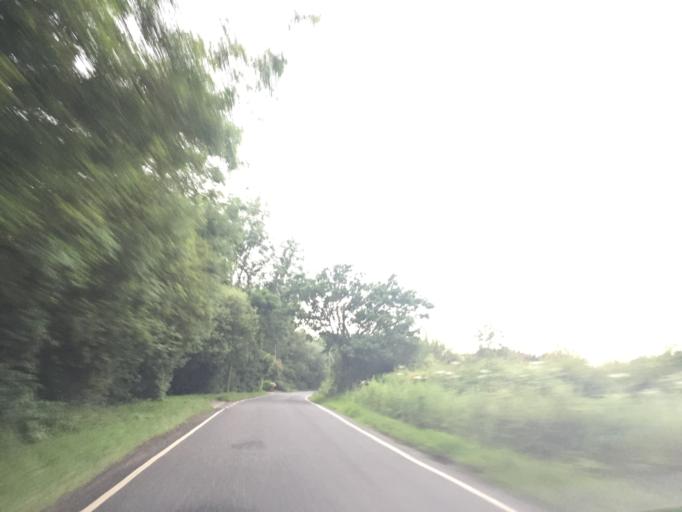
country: GB
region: England
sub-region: Essex
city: Hatfield Heath
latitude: 51.7600
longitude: 0.1804
